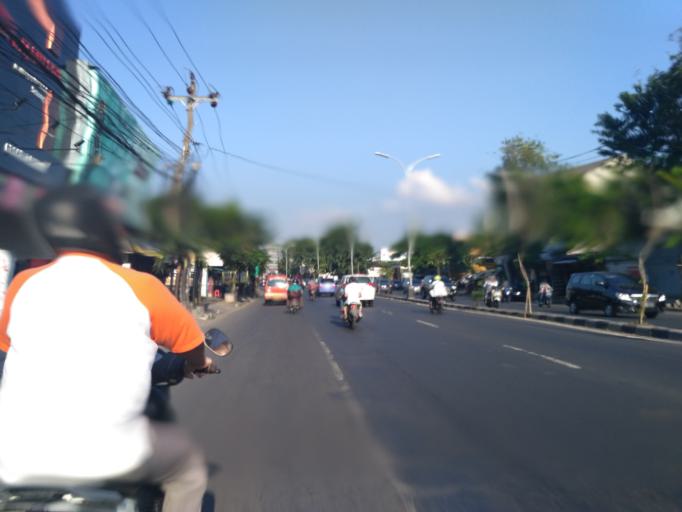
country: ID
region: Central Java
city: Semarang
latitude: -7.0047
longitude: 110.4528
